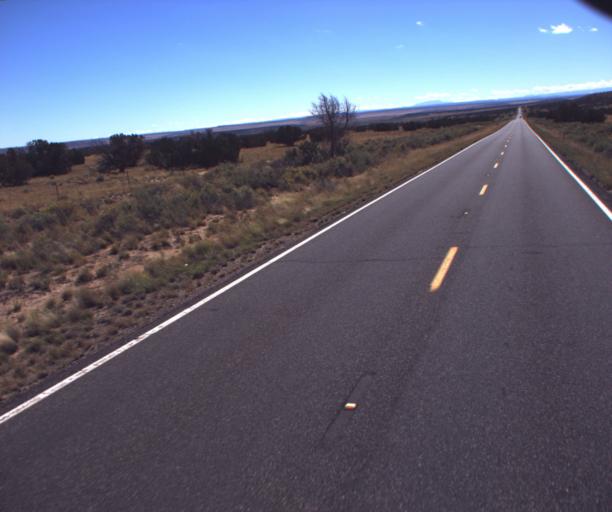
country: US
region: Arizona
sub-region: Apache County
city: Saint Johns
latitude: 34.8101
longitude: -109.2378
